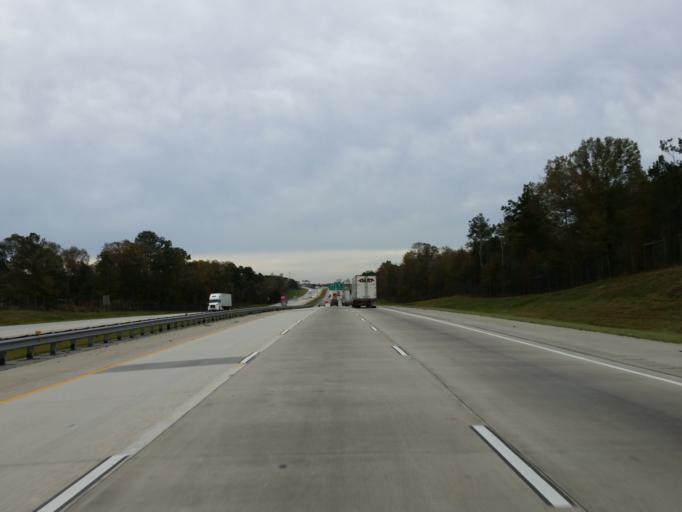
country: US
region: Georgia
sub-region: Dooly County
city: Unadilla
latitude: 32.2739
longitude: -83.7539
